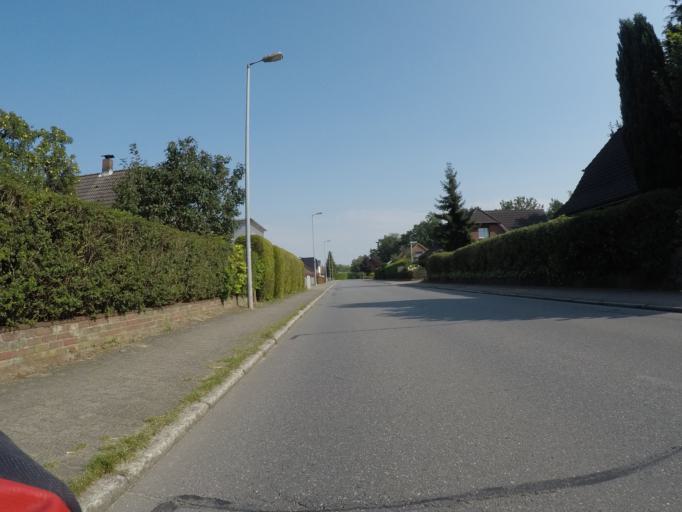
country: DE
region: Schleswig-Holstein
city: Wahlstedt
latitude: 53.9515
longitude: 10.2179
